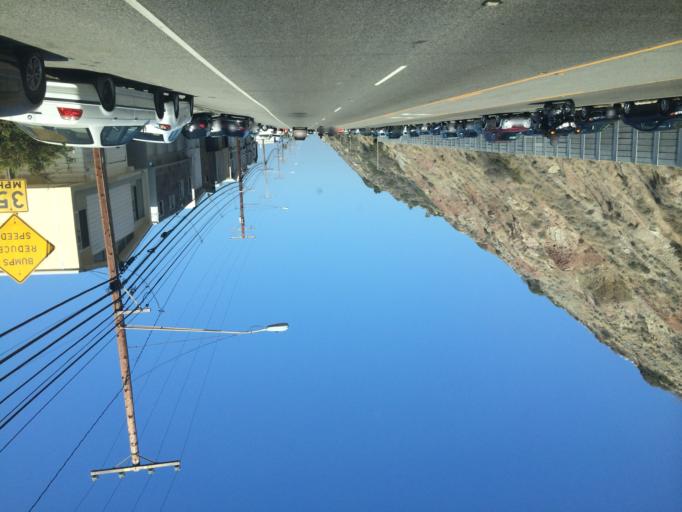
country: US
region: California
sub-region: Los Angeles County
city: Las Flores
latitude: 34.0380
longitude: -118.6213
